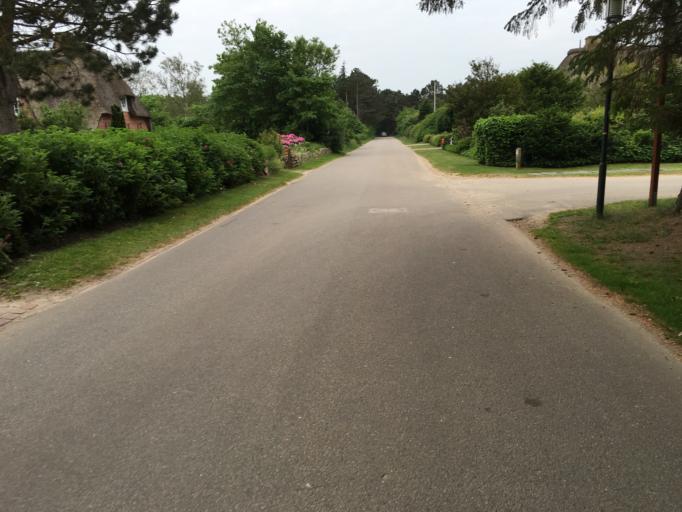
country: DE
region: Schleswig-Holstein
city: Norddorf
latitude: 54.6747
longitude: 8.3348
